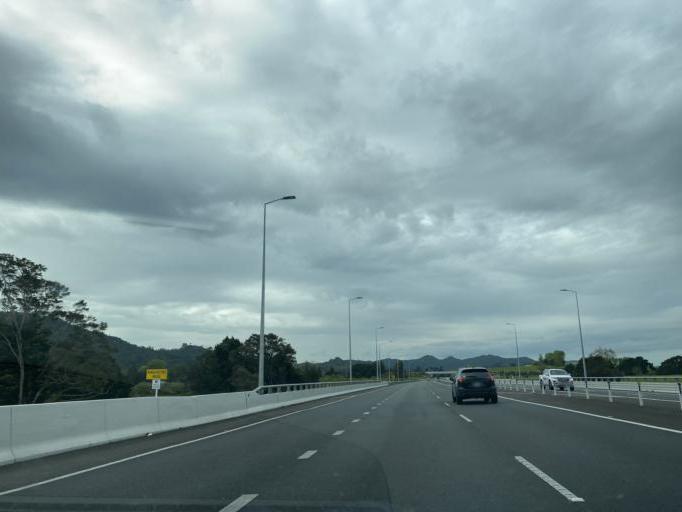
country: NZ
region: Waikato
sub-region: Waikato District
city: Ngaruawahia
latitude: -37.6186
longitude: 175.2050
